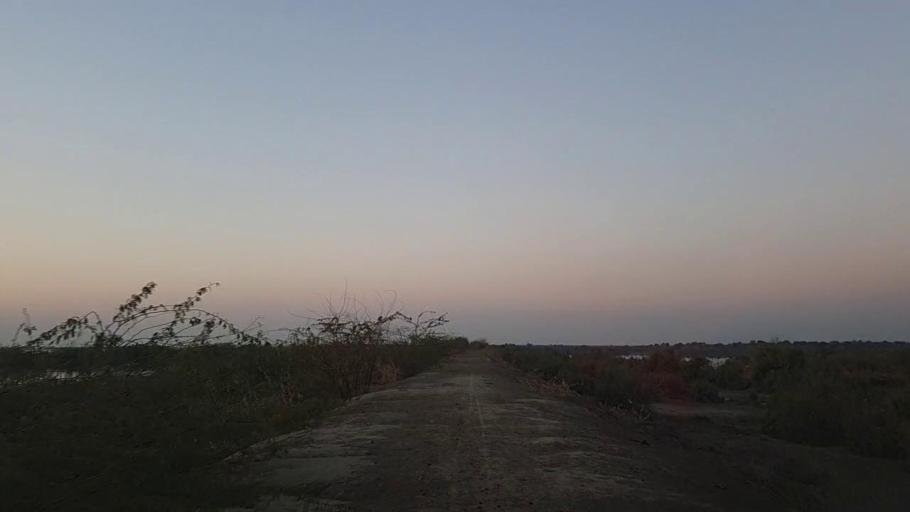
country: PK
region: Sindh
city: Tando Mittha Khan
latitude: 26.0784
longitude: 69.1529
